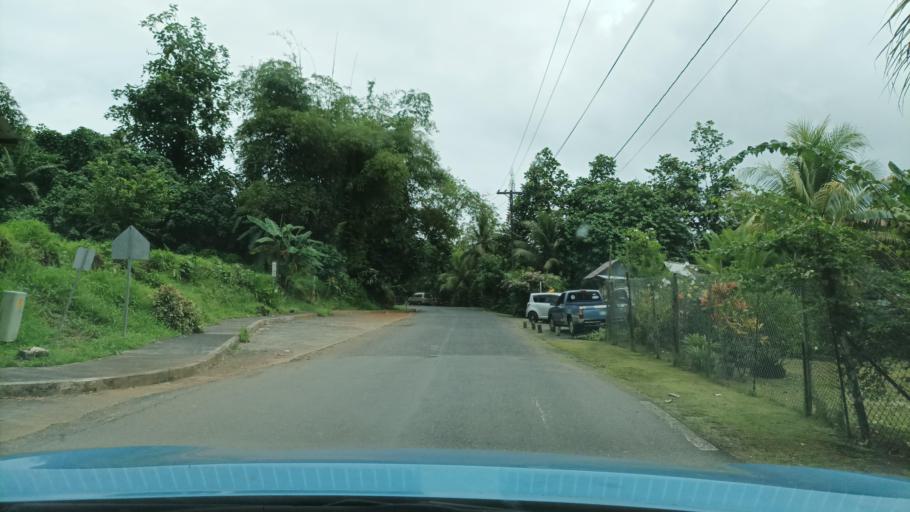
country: FM
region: Pohnpei
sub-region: Kolonia Municipality
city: Kolonia
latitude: 6.9352
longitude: 158.2784
